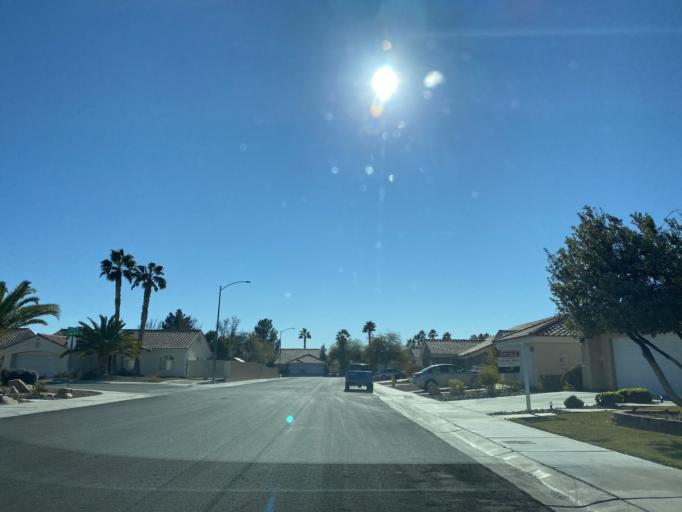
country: US
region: Nevada
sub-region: Clark County
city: Summerlin South
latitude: 36.2646
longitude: -115.2742
